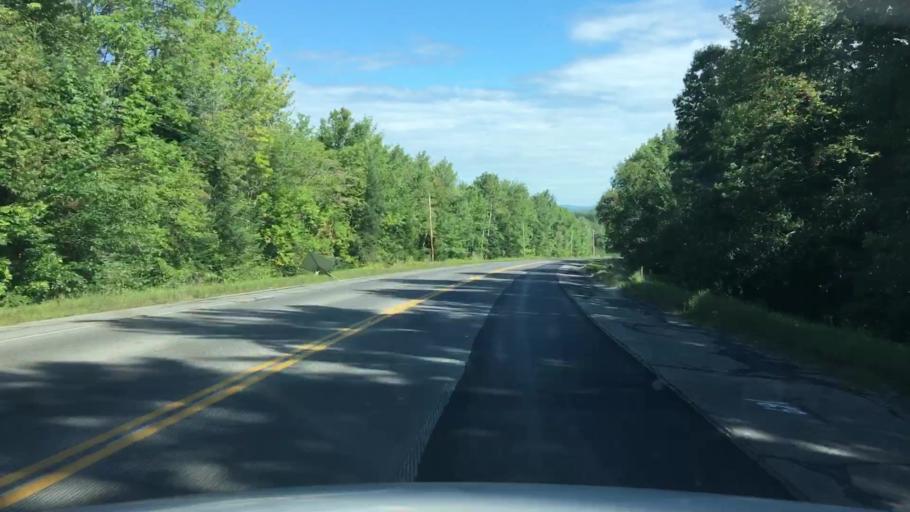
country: US
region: Maine
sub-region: Penobscot County
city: Newport
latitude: 44.8793
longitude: -69.2814
